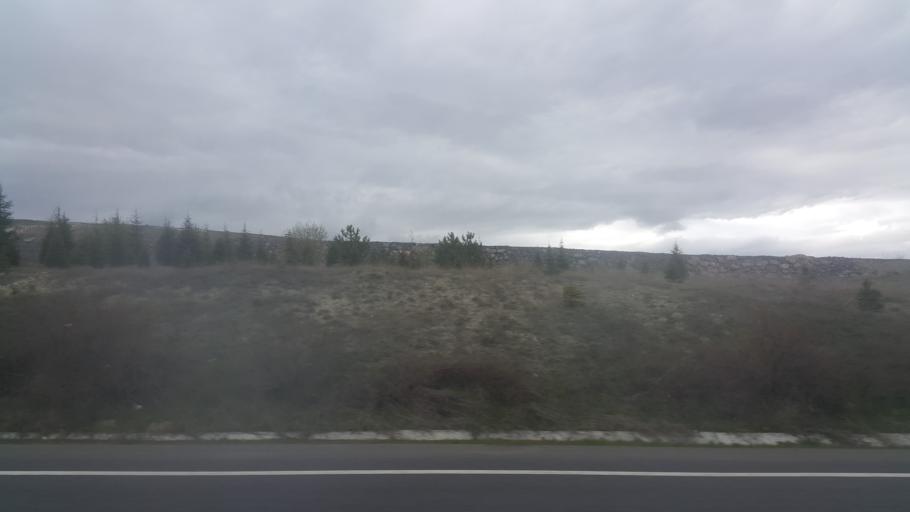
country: TR
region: Ankara
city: Etimesgut
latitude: 39.8999
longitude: 32.6229
